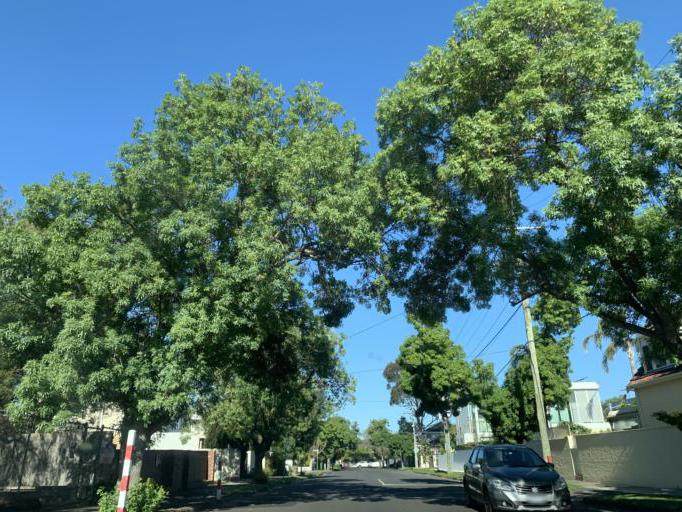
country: AU
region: Victoria
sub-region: Bayside
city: Hampton
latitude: -37.9227
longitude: 144.9966
